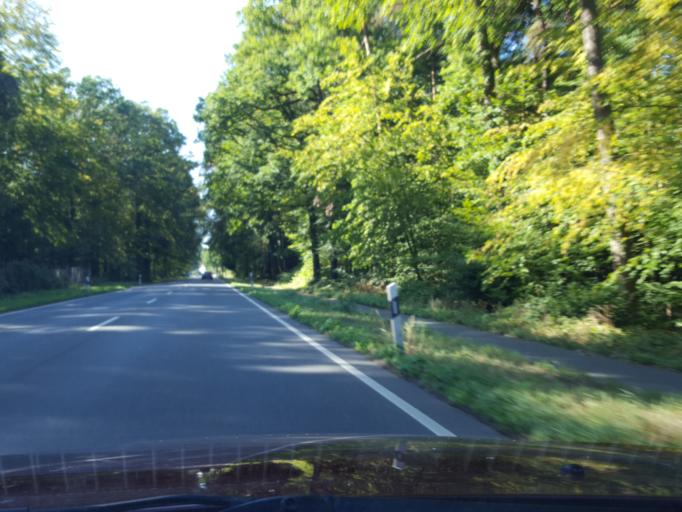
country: DE
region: Lower Saxony
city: Dorverden
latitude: 52.8230
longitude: 9.2029
